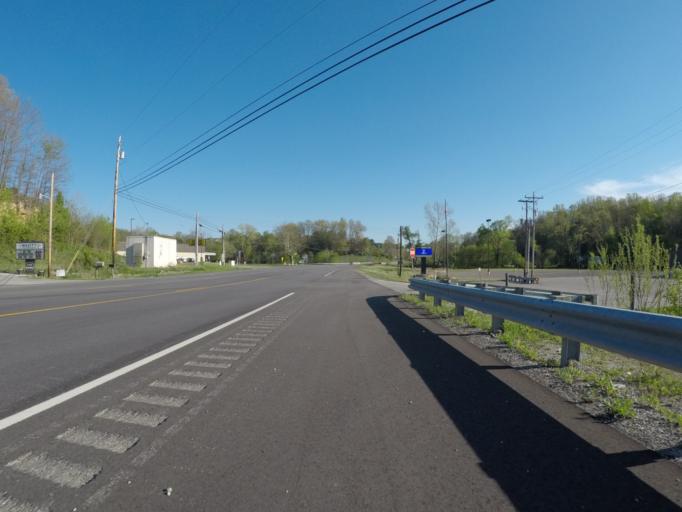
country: US
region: Kentucky
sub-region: Boyd County
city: Meads
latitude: 38.3582
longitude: -82.6974
